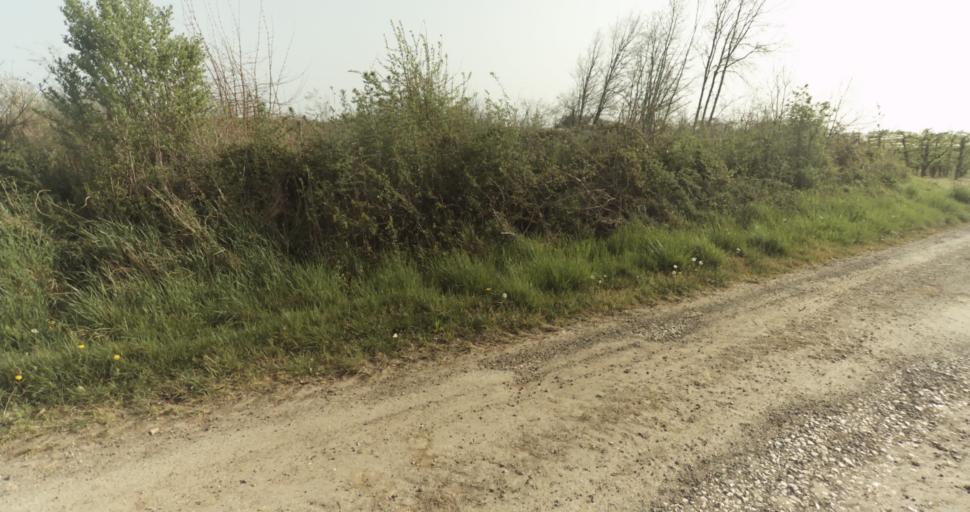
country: FR
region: Midi-Pyrenees
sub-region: Departement du Tarn-et-Garonne
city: Moissac
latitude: 44.1486
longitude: 1.0586
